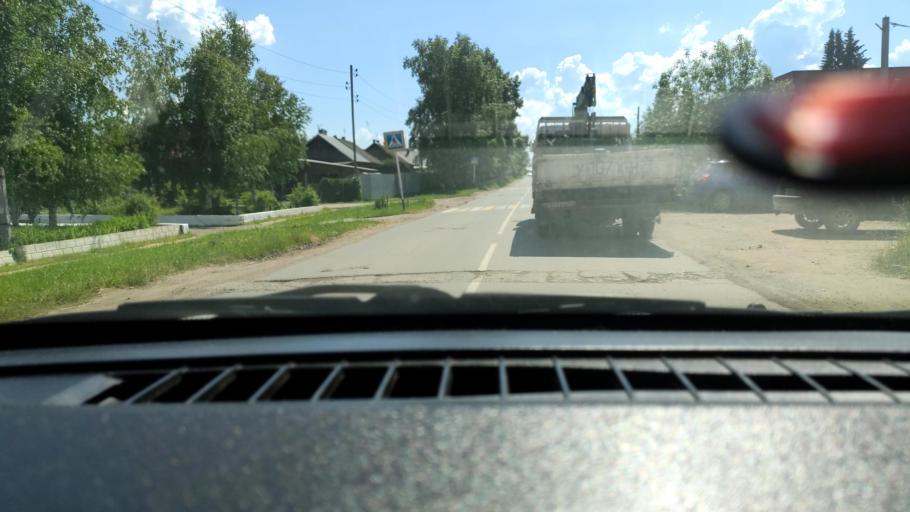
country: RU
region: Perm
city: Sylva
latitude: 58.0331
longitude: 56.7595
